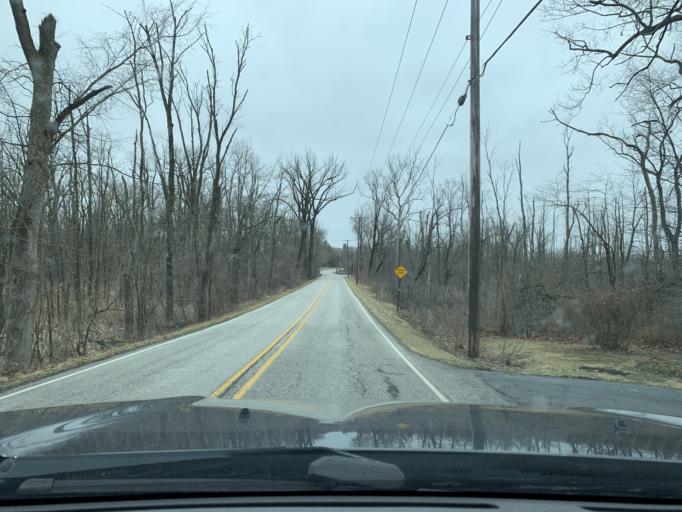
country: US
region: Indiana
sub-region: Porter County
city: Chesterton
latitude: 41.6137
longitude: -87.0166
